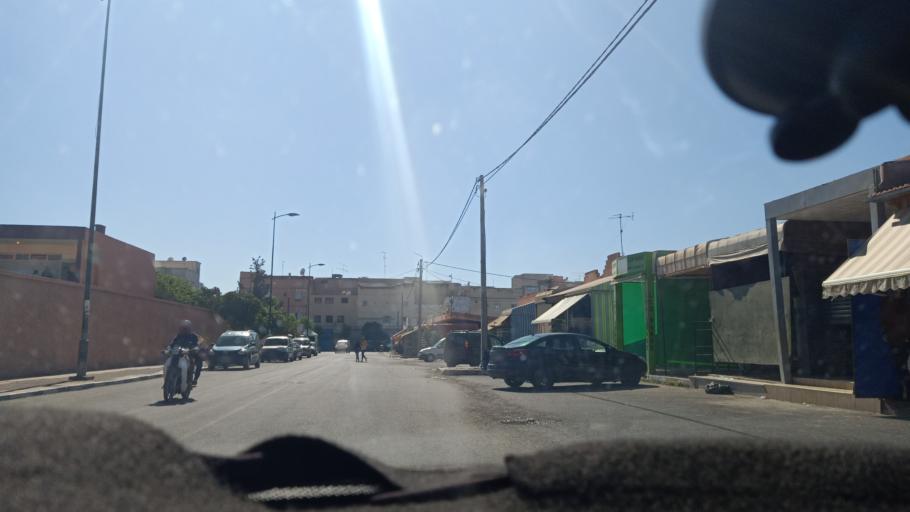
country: MA
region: Doukkala-Abda
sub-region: Safi
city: Youssoufia
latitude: 32.2429
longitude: -8.5351
